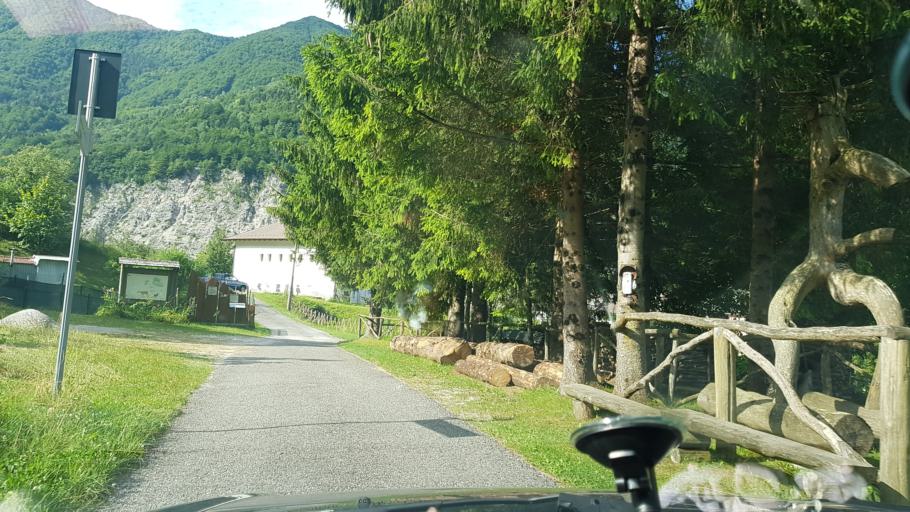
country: IT
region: Friuli Venezia Giulia
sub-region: Provincia di Udine
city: Prato
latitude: 46.3482
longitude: 13.3941
